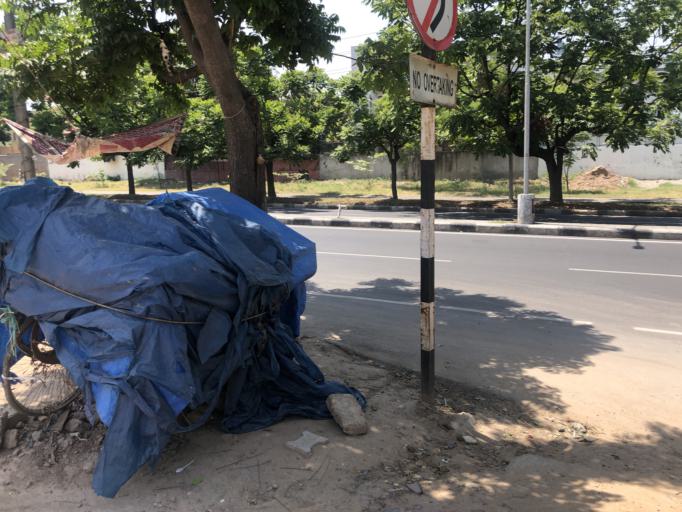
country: IN
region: Chandigarh
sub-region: Chandigarh
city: Chandigarh
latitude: 30.7106
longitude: 76.7721
